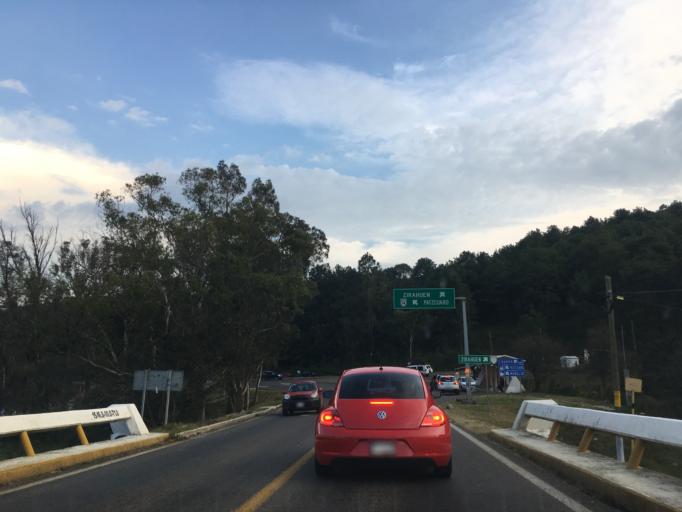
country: MX
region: Michoacan
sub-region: Patzcuaro
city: Santa Maria Huiramangaro (San Juan Tumbio)
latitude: 19.4836
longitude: -101.7402
